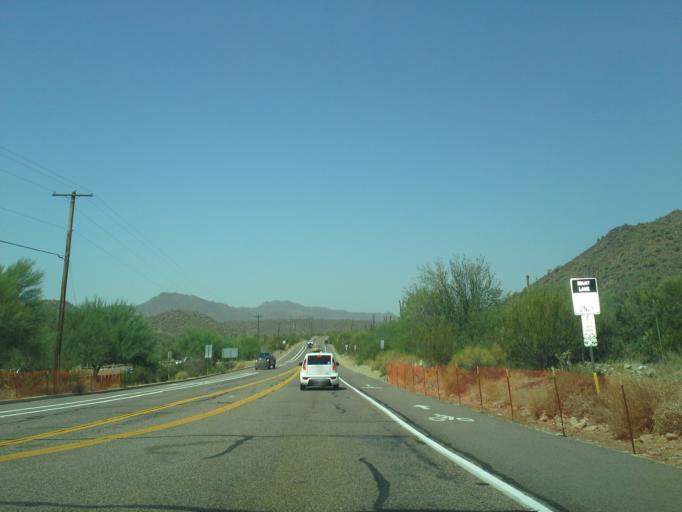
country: US
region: Arizona
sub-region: Pinal County
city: Apache Junction
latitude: 33.5562
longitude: -111.5435
